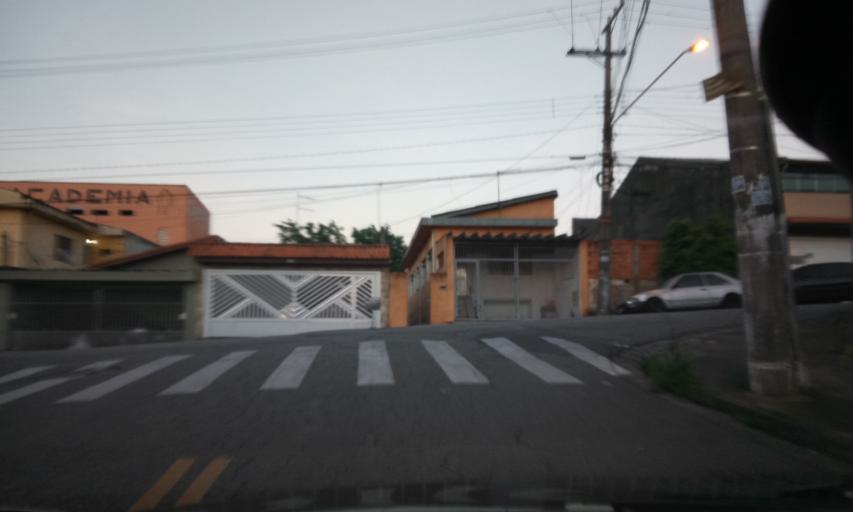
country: BR
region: Sao Paulo
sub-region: Sao Bernardo Do Campo
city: Sao Bernardo do Campo
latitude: -23.7264
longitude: -46.5694
